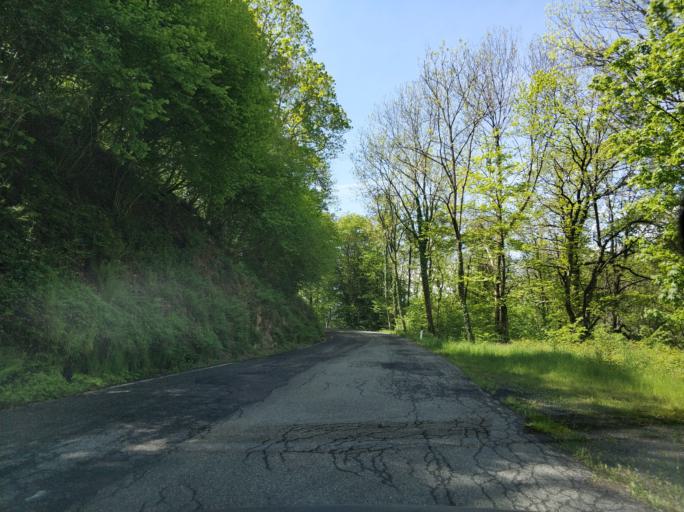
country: IT
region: Piedmont
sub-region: Provincia di Torino
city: Coassolo
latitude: 45.3152
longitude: 7.4730
